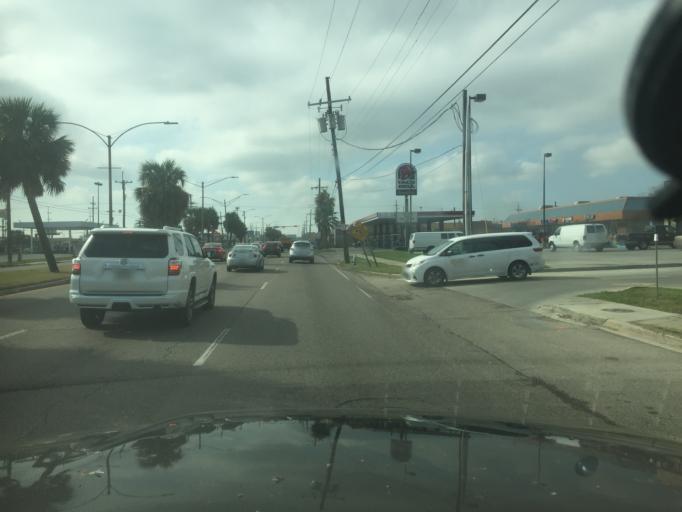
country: US
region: Louisiana
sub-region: Saint Bernard Parish
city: Arabi
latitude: 30.0060
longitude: -90.0349
